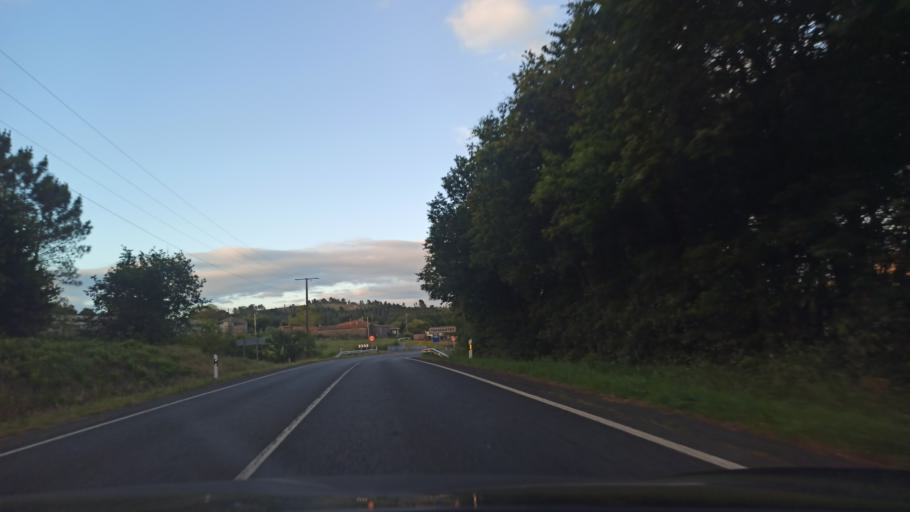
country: ES
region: Galicia
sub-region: Provincia de Pontevedra
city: Rodeiro
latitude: 42.7682
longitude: -7.9847
